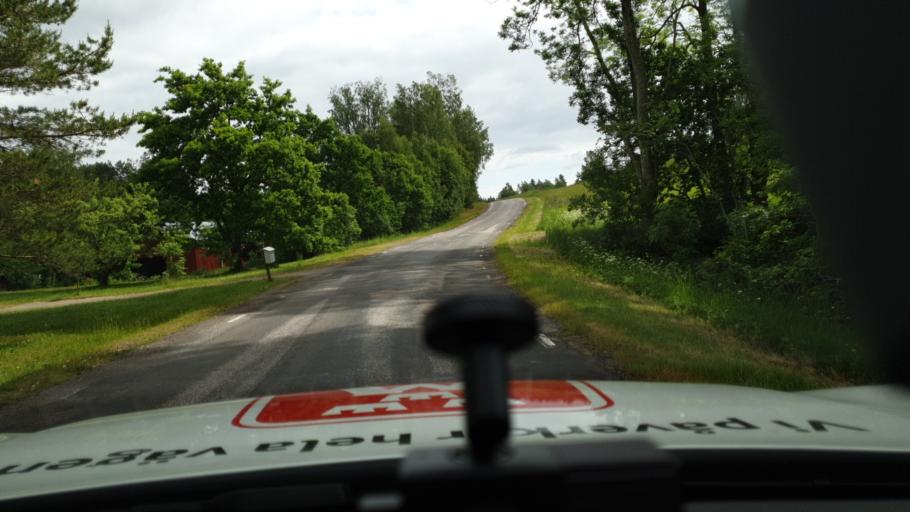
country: SE
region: Vaestra Goetaland
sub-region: Hjo Kommun
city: Hjo
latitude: 58.4035
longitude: 14.2959
